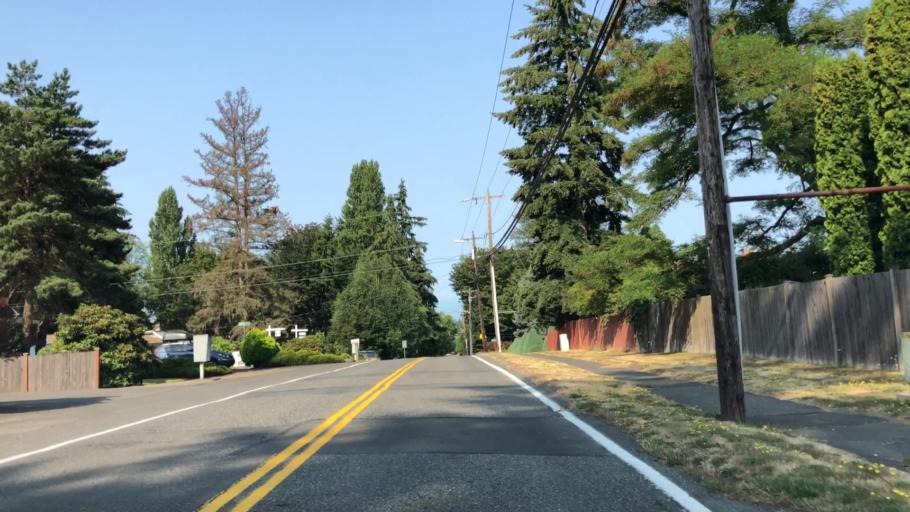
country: US
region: Washington
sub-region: Snohomish County
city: Alderwood Manor
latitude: 47.8429
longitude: -122.2858
